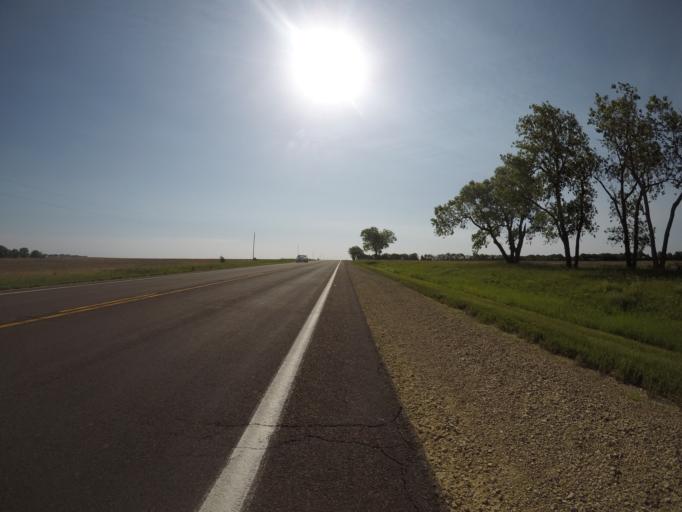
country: US
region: Kansas
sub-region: Riley County
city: Fort Riley North
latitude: 39.3068
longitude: -96.9148
